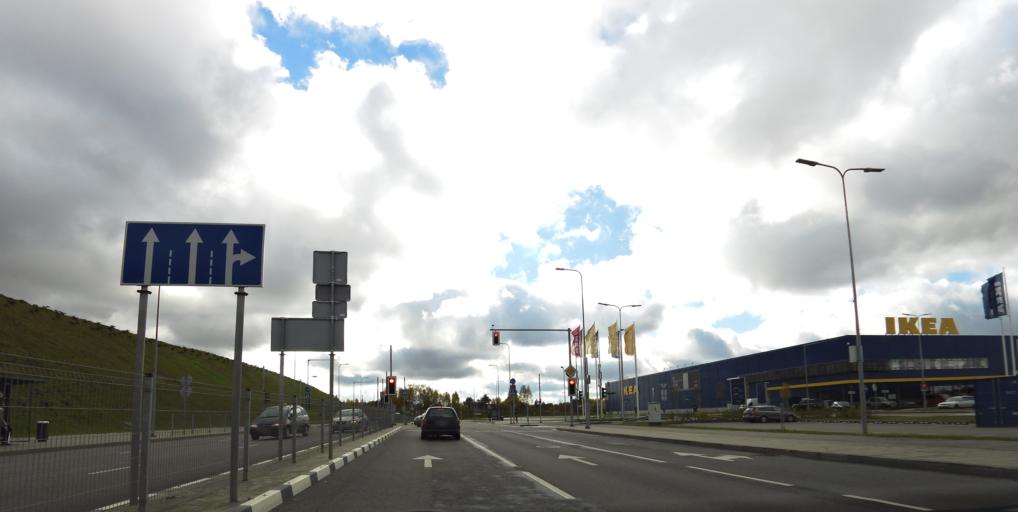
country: LT
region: Vilnius County
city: Naujamiestis
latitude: 54.6521
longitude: 25.2823
